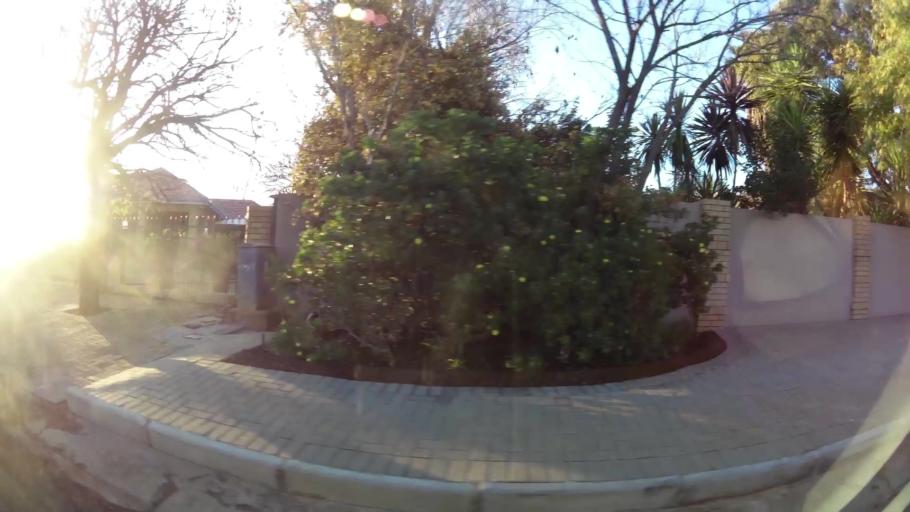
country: ZA
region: Orange Free State
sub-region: Mangaung Metropolitan Municipality
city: Bloemfontein
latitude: -29.0911
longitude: 26.1536
